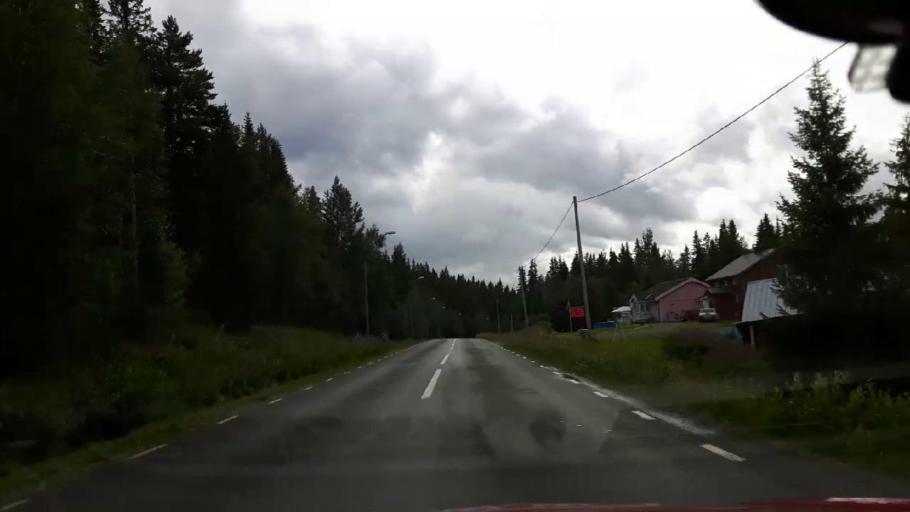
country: NO
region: Nord-Trondelag
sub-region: Lierne
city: Sandvika
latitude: 64.5051
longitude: 14.1570
